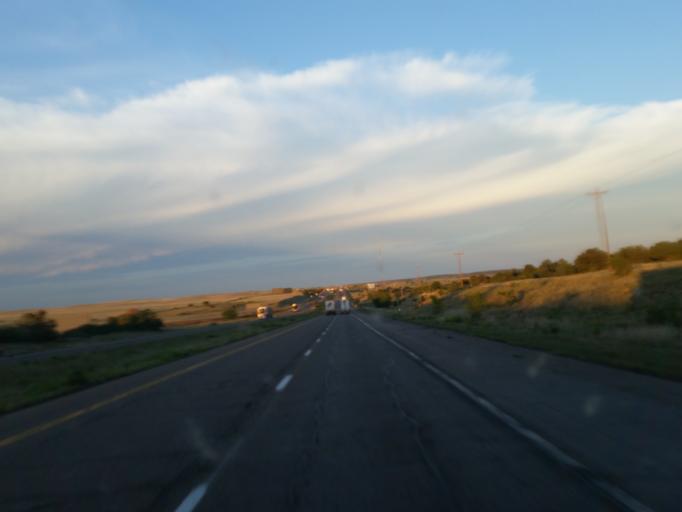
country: US
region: New Mexico
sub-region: San Miguel County
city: Las Vegas
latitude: 34.9922
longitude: -105.3118
